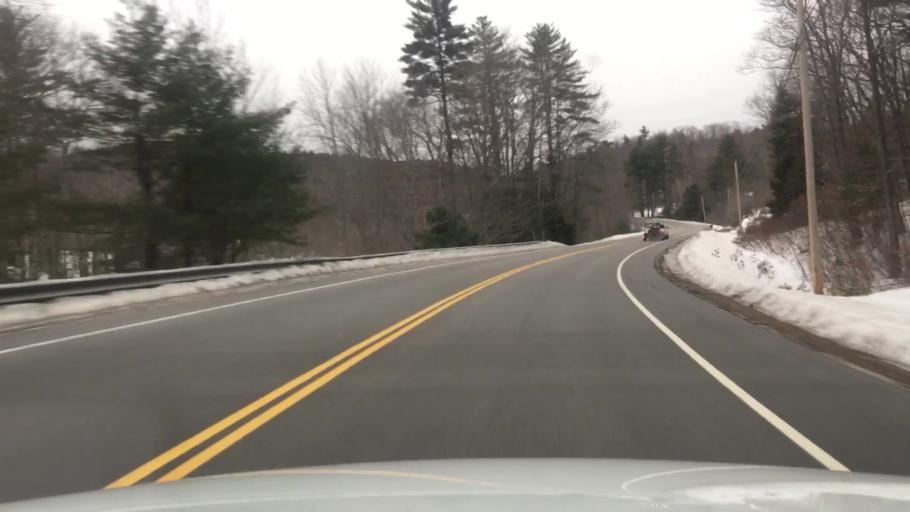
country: US
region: Maine
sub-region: York County
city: Limerick
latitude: 43.7301
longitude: -70.8160
